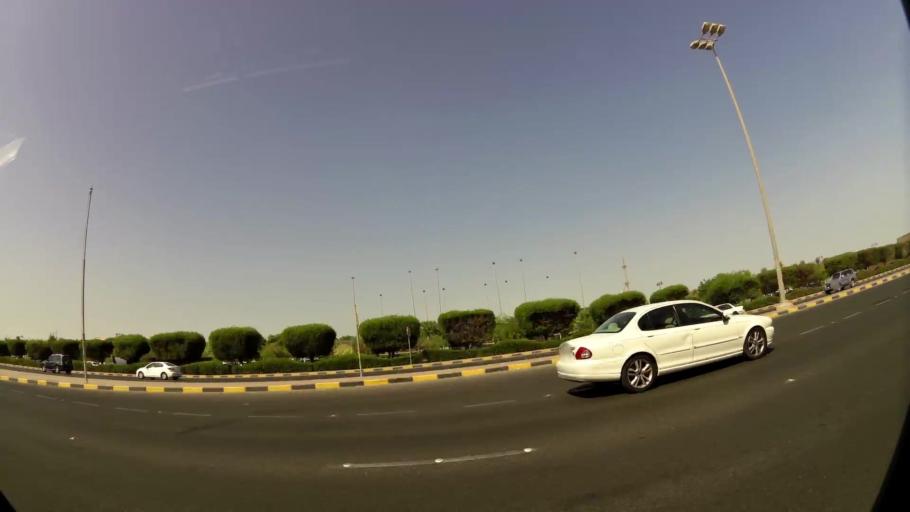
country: KW
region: Muhafazat Hawalli
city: As Salimiyah
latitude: 29.3419
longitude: 48.0681
